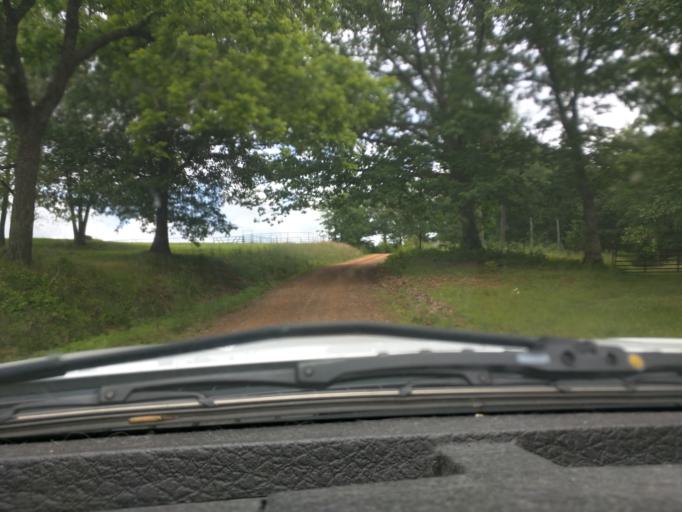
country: US
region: Arkansas
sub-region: Madison County
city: Huntsville
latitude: 35.8914
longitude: -93.5720
